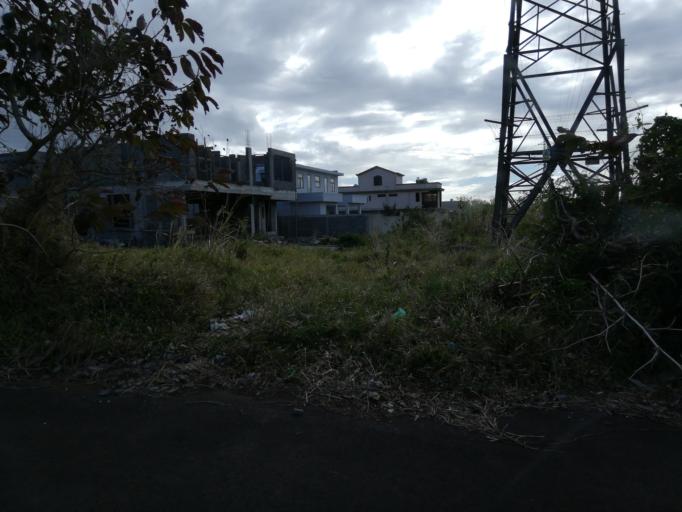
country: MU
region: Plaines Wilhems
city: Ebene
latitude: -20.2450
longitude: 57.4856
